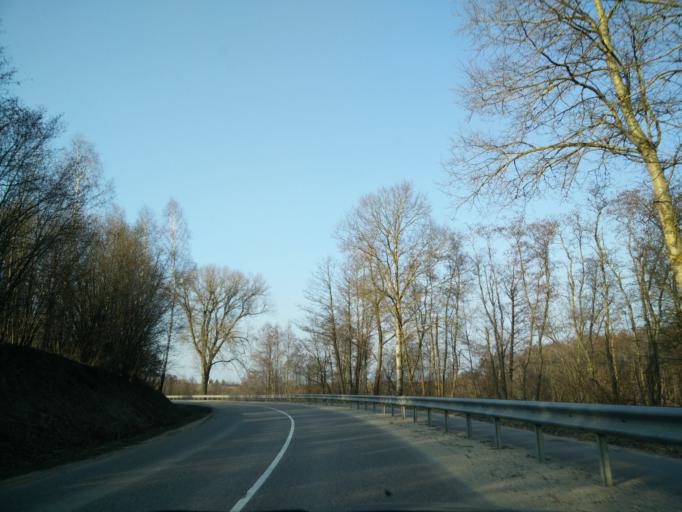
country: LT
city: Trakai
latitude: 54.6688
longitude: 24.9131
